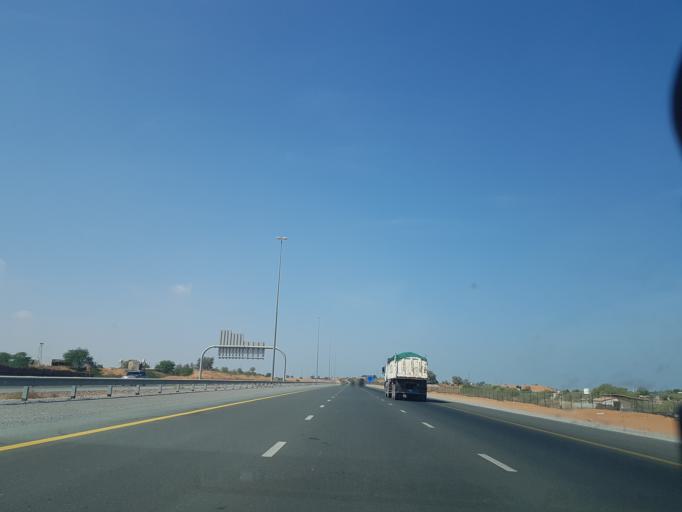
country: AE
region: Ra's al Khaymah
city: Ras al-Khaimah
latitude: 25.7042
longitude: 55.9536
